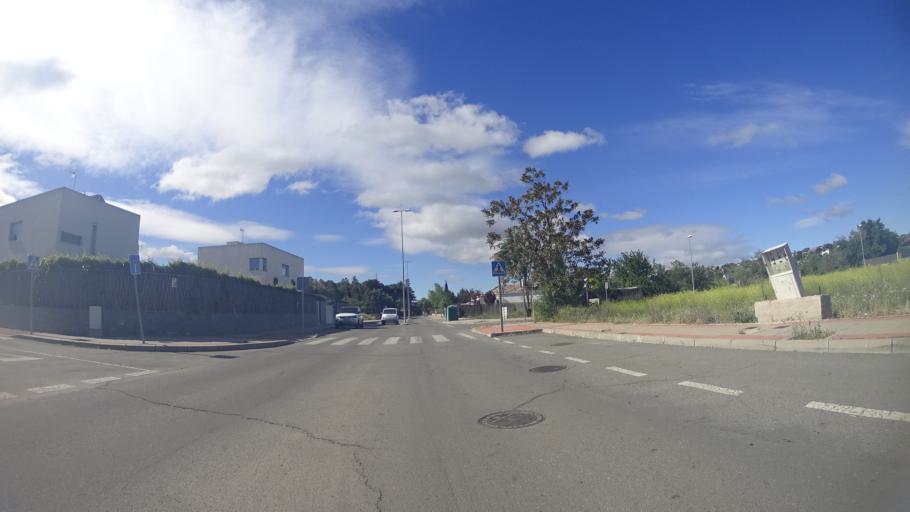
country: ES
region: Madrid
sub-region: Provincia de Madrid
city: Villanueva del Pardillo
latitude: 40.4877
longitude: -3.9396
